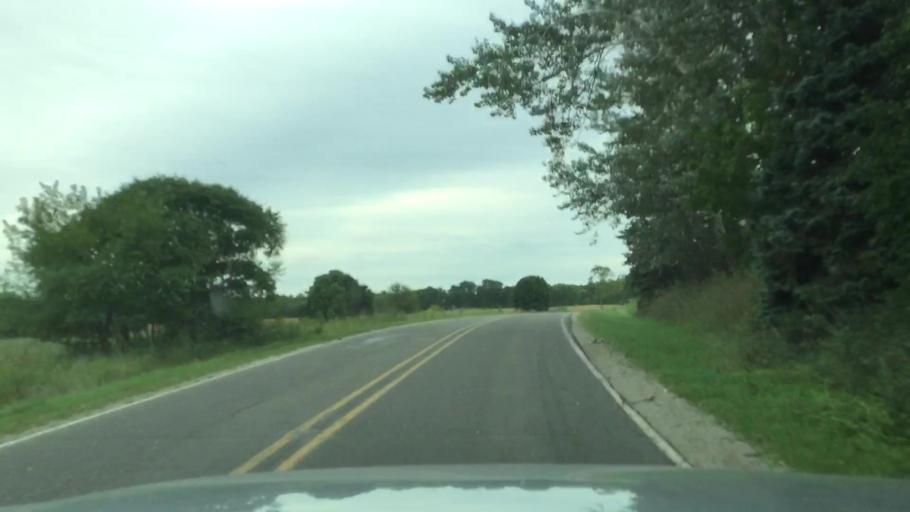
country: US
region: Michigan
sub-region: Shiawassee County
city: Durand
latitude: 42.8563
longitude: -84.0394
